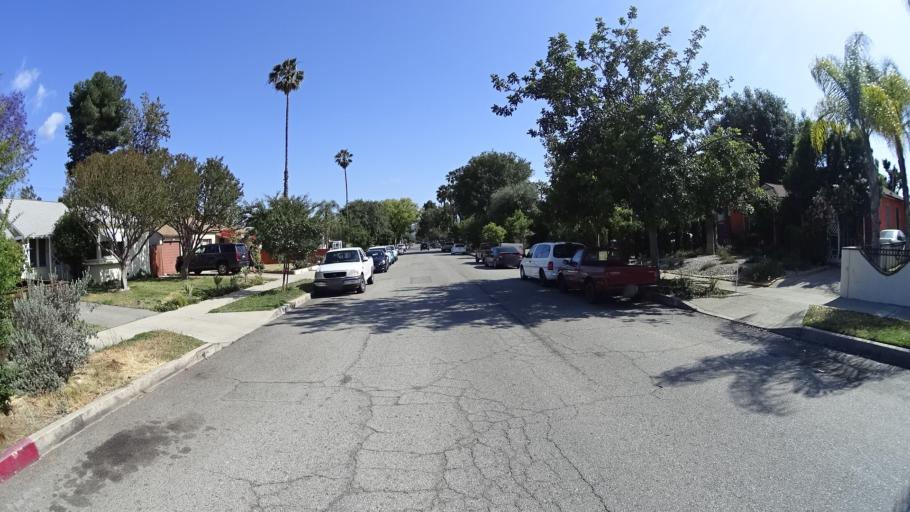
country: US
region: California
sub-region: Los Angeles County
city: North Hollywood
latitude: 34.1756
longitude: -118.3639
